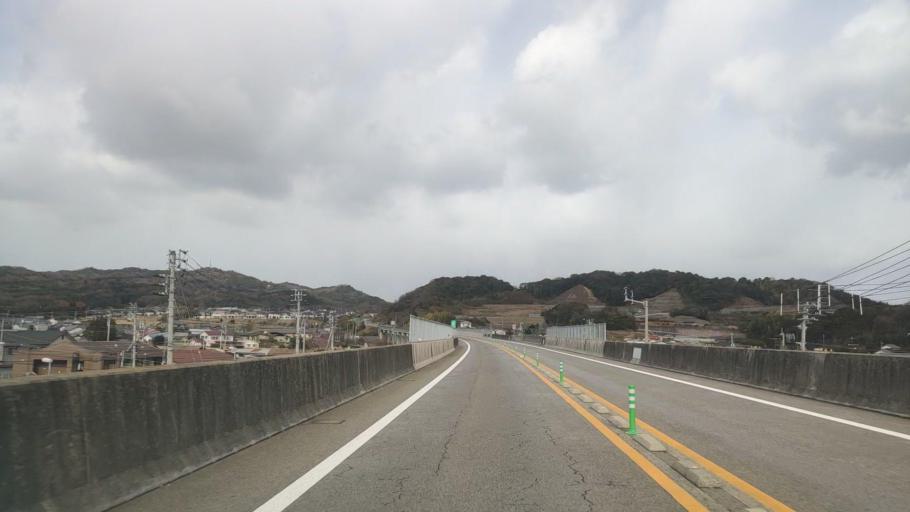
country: JP
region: Ehime
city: Hojo
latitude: 34.0603
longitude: 132.9721
